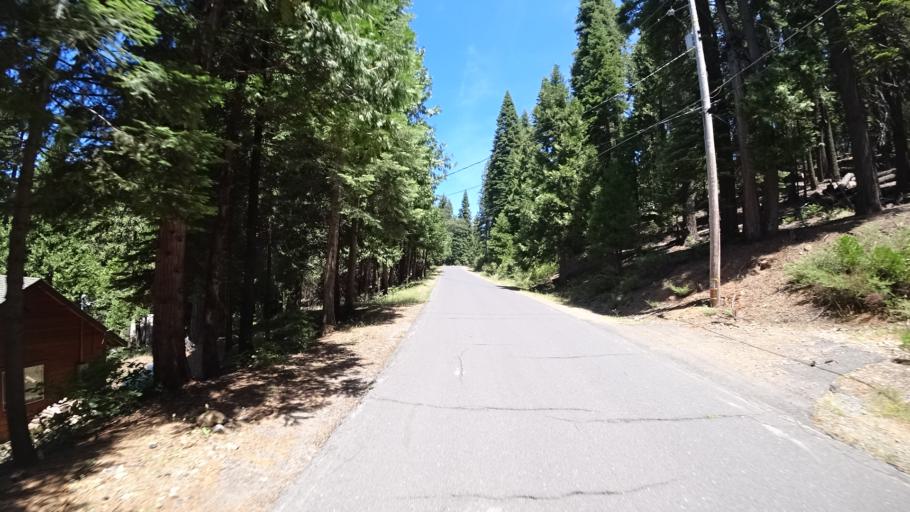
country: US
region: California
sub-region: Calaveras County
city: Arnold
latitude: 38.3137
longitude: -120.2616
